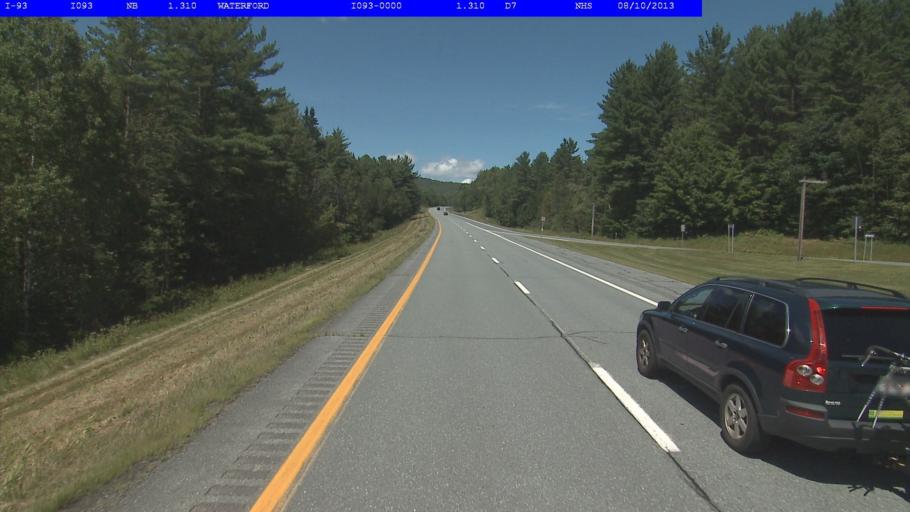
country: US
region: Vermont
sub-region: Caledonia County
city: Saint Johnsbury
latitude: 44.3612
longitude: -71.8986
